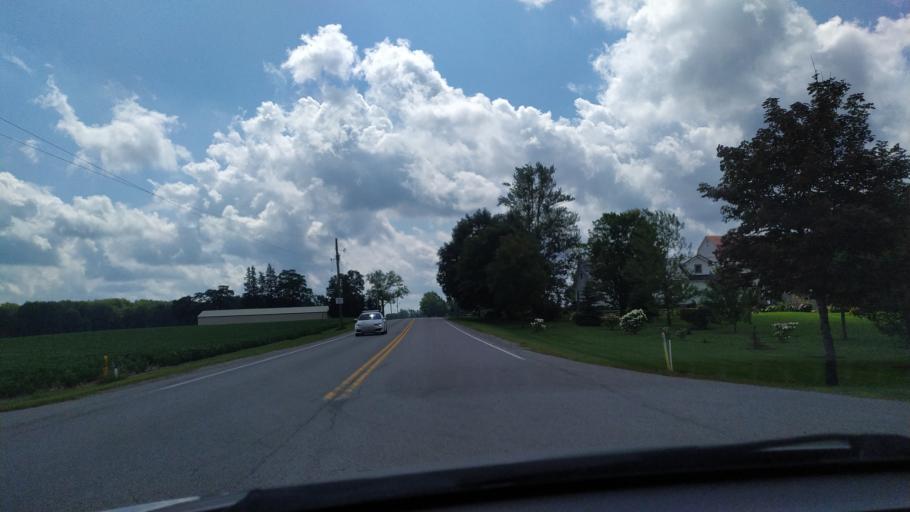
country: CA
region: Ontario
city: London
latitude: 43.0662
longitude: -81.3352
